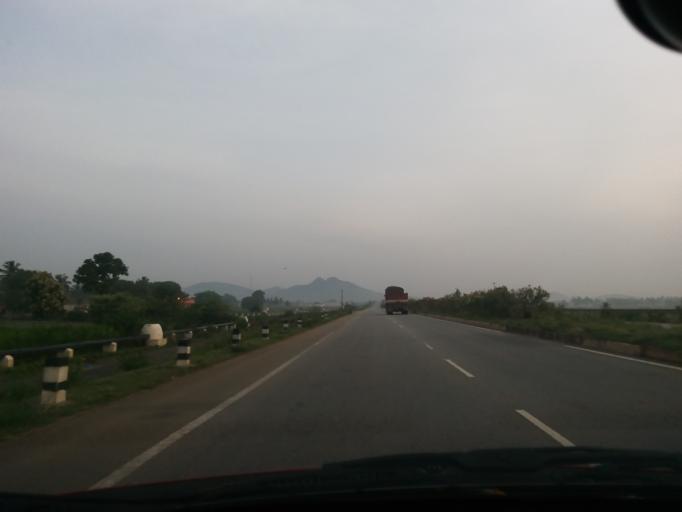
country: IN
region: Karnataka
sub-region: Chikkaballapur
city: Chik Ballapur
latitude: 13.4258
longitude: 77.7437
